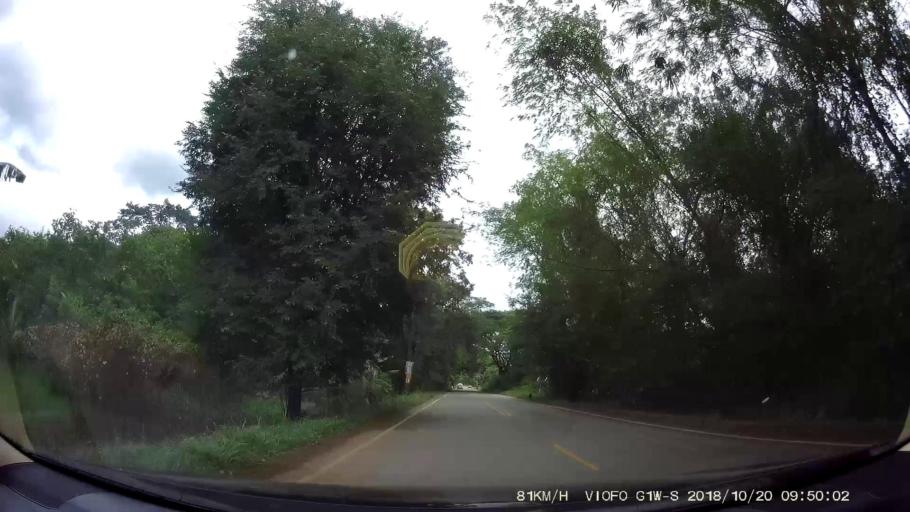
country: TH
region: Chaiyaphum
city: Khon San
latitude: 16.5267
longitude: 101.9033
